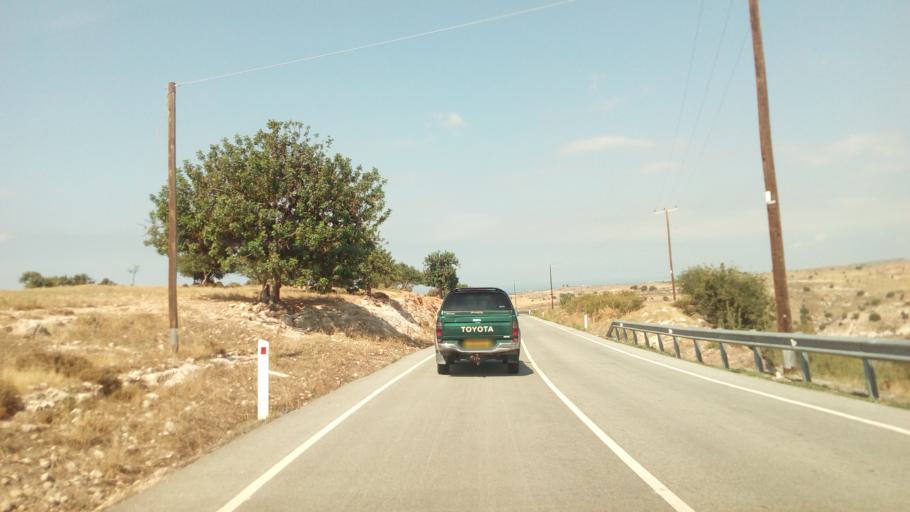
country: CY
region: Limassol
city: Pissouri
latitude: 34.7393
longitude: 32.5800
